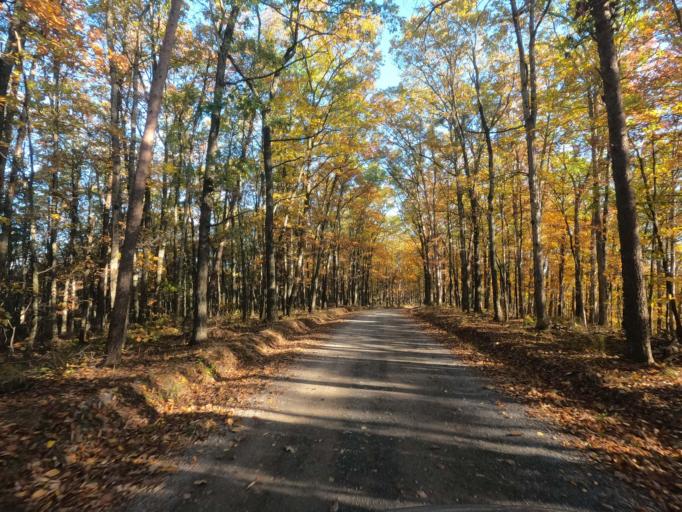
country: US
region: West Virginia
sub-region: Morgan County
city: Berkeley Springs
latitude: 39.6543
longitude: -78.4634
